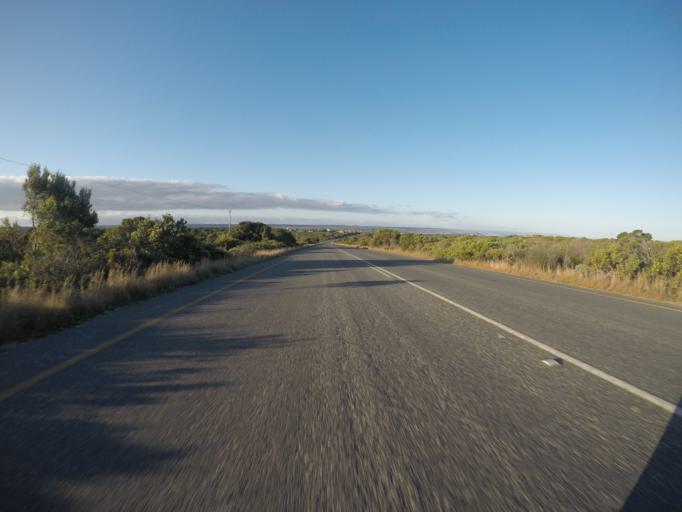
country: ZA
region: Western Cape
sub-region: Eden District Municipality
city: Riversdale
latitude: -34.3915
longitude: 21.3960
